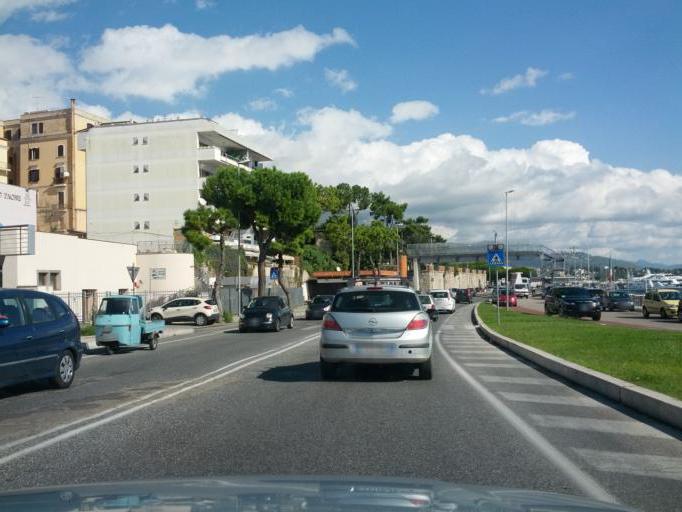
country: IT
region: Latium
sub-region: Provincia di Latina
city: Formia
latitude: 41.2549
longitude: 13.6072
